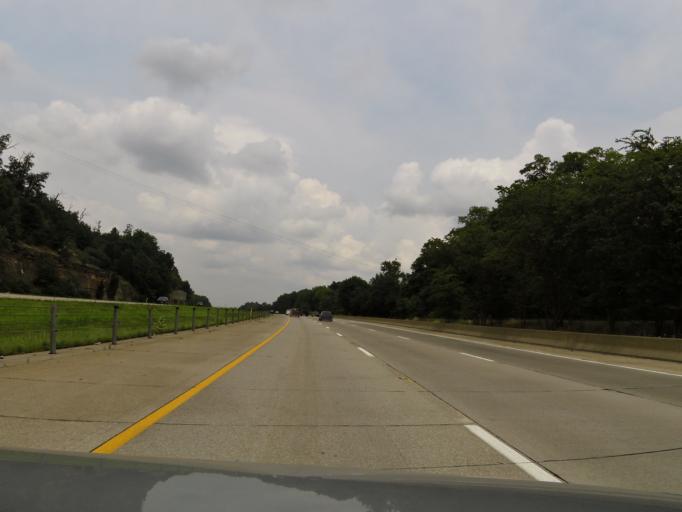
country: US
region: Kentucky
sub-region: Bullitt County
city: Shepherdsville
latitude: 38.0119
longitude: -85.6969
